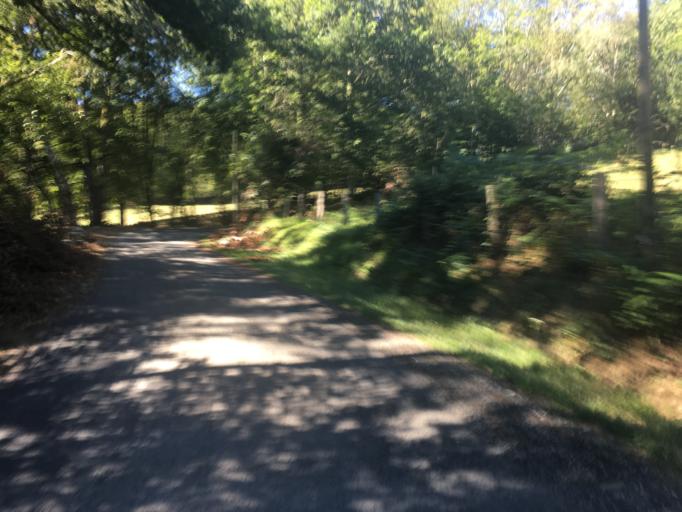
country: FR
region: Limousin
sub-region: Departement de la Correze
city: Bort-les-Orgues
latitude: 45.4030
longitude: 2.4841
